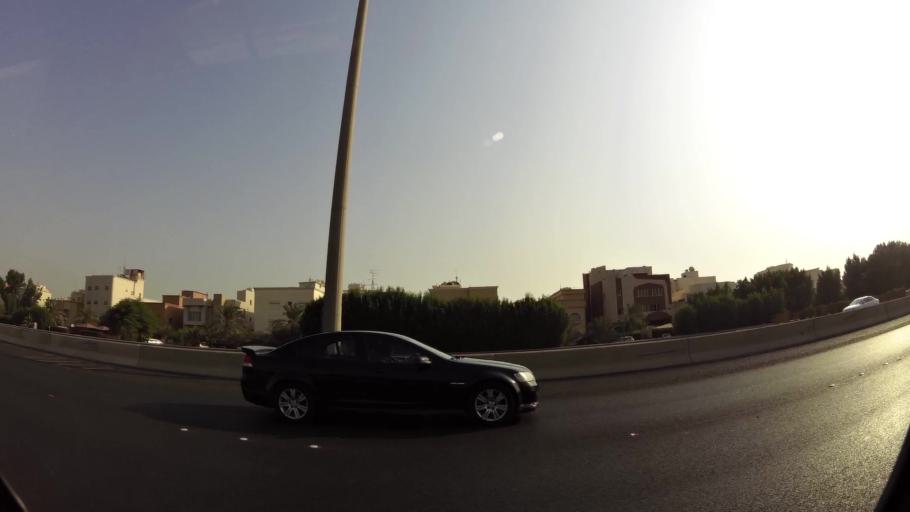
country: KW
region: Muhafazat Hawalli
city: Salwa
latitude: 29.2733
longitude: 48.0825
